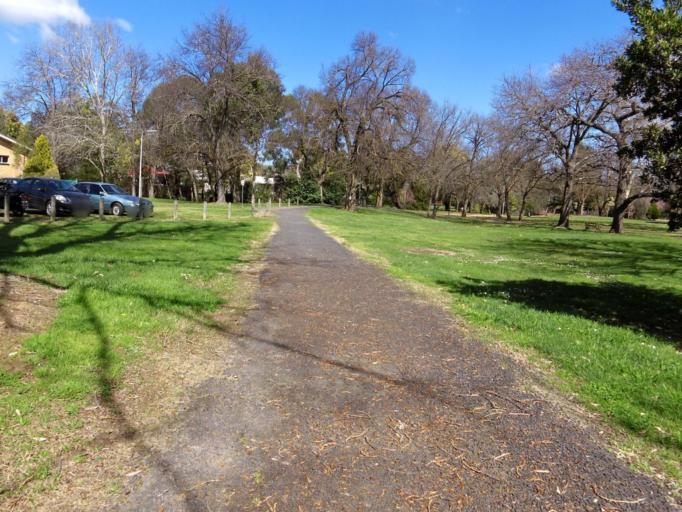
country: AU
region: Victoria
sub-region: Murrindindi
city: Alexandra
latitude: -37.1888
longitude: 145.7106
